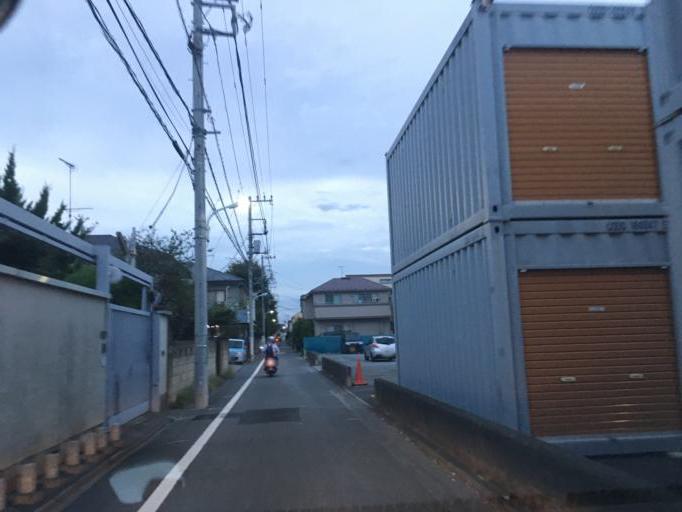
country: JP
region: Tokyo
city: Kokubunji
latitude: 35.7132
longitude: 139.4554
